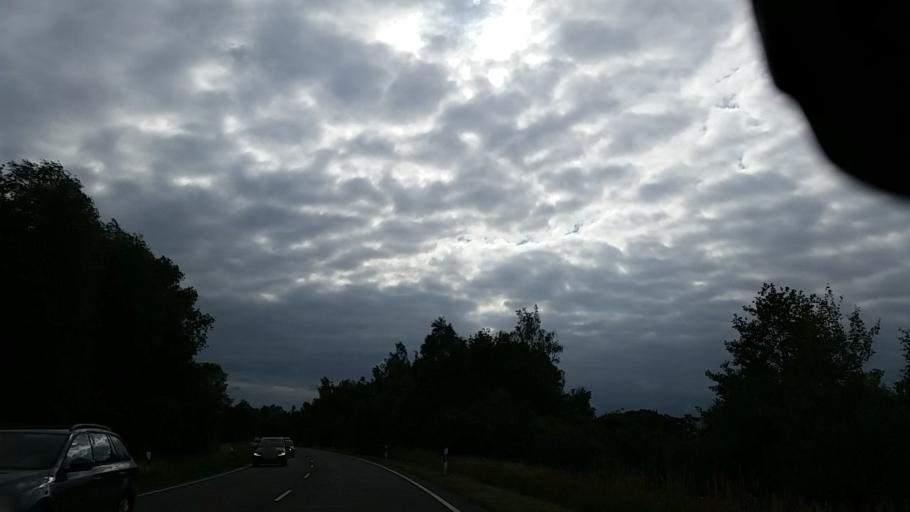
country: DE
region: Lower Saxony
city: Wolfsburg
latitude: 52.4269
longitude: 10.8377
